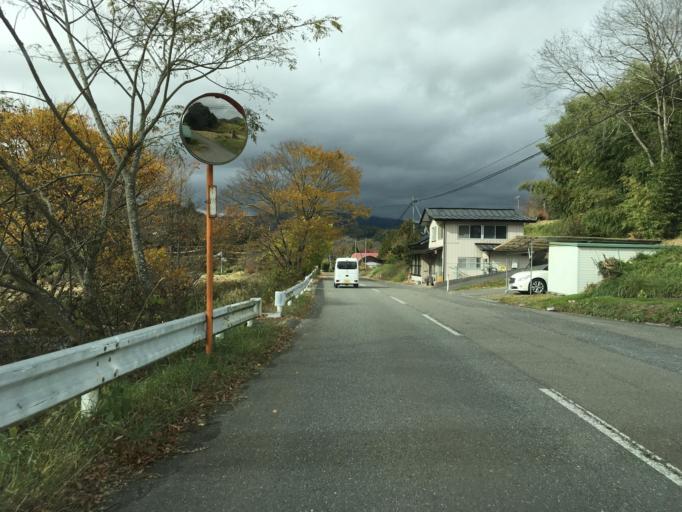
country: JP
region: Iwate
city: Mizusawa
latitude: 39.0622
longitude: 141.3898
